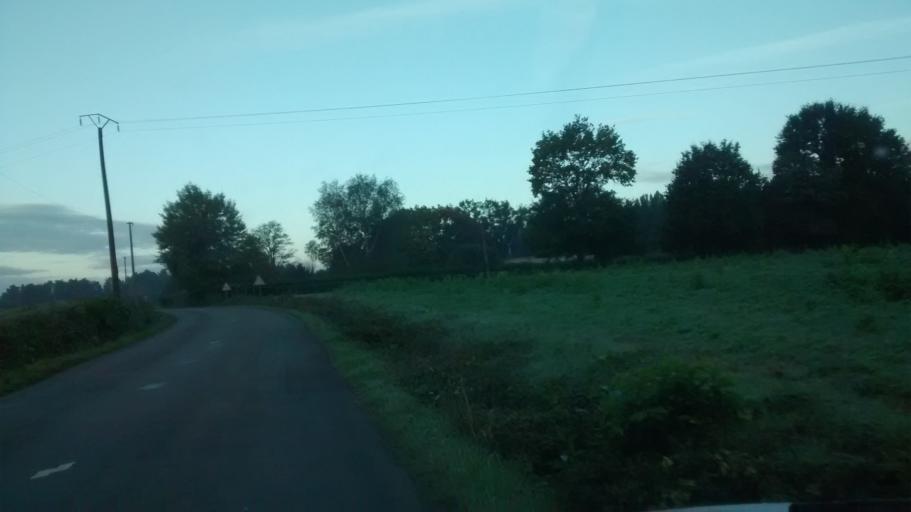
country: FR
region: Brittany
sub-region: Departement d'Ille-et-Vilaine
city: Melesse
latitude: 48.1959
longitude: -1.6887
